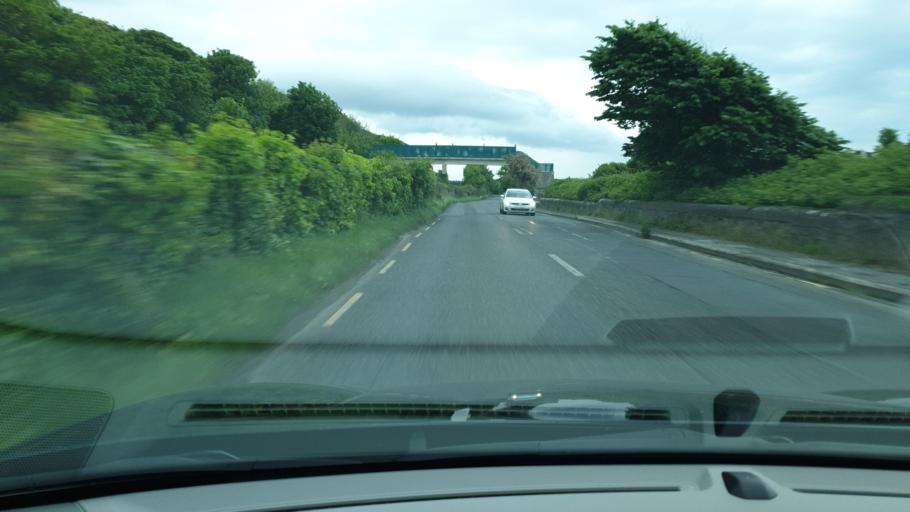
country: IE
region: Leinster
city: Balrothery
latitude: 53.5903
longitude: -6.1552
